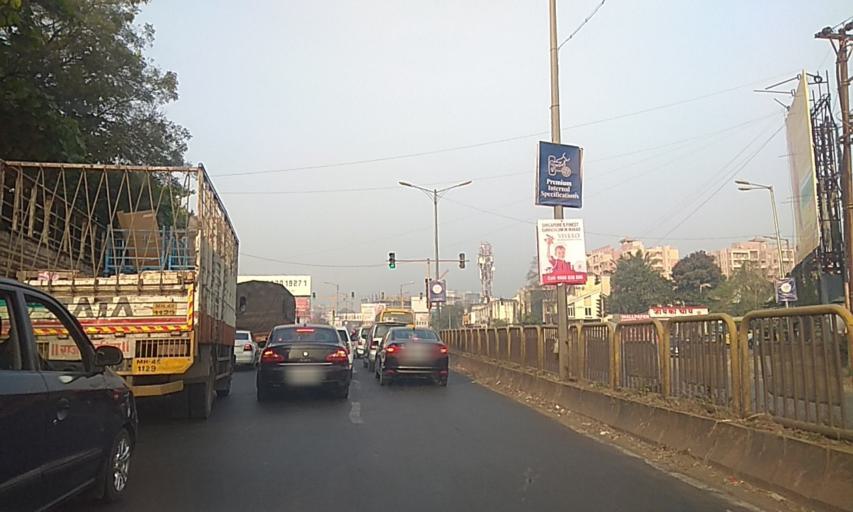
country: IN
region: Maharashtra
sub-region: Pune Division
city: Pimpri
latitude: 18.5922
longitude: 73.7633
